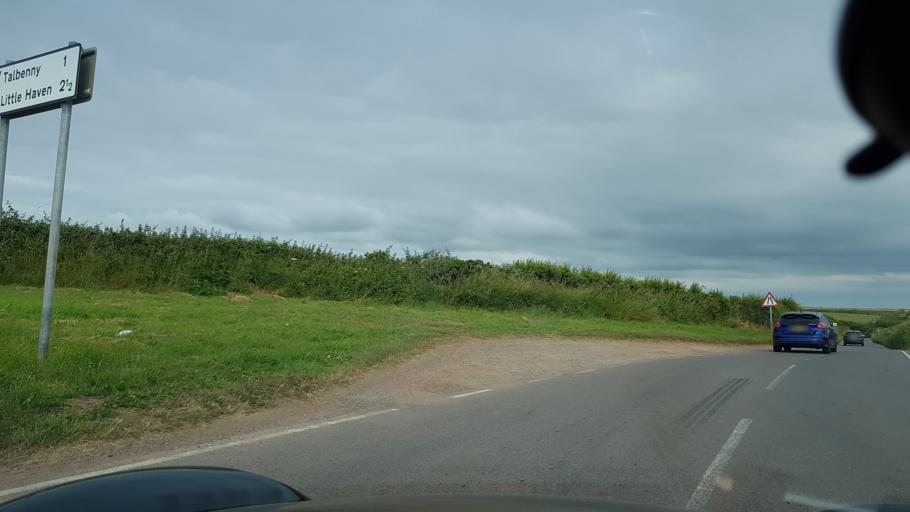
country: GB
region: Wales
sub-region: Pembrokeshire
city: Dale
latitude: 51.7500
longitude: -5.1405
